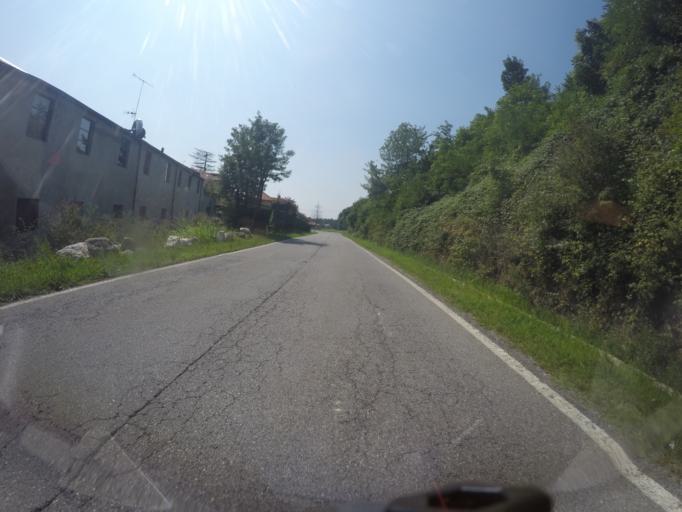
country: IT
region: Lombardy
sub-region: Provincia di Lecco
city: Olgiate Molgora
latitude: 45.7350
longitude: 9.3883
